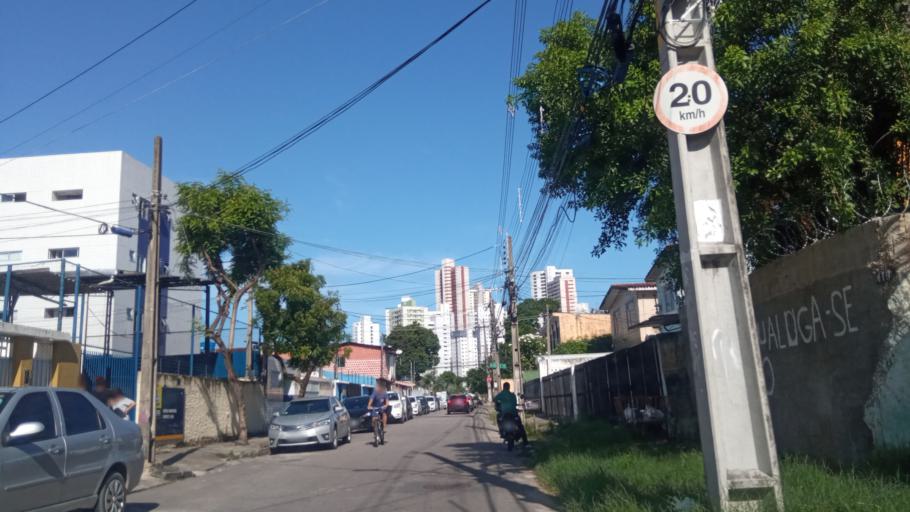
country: BR
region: Pernambuco
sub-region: Recife
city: Recife
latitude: -8.0287
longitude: -34.9007
